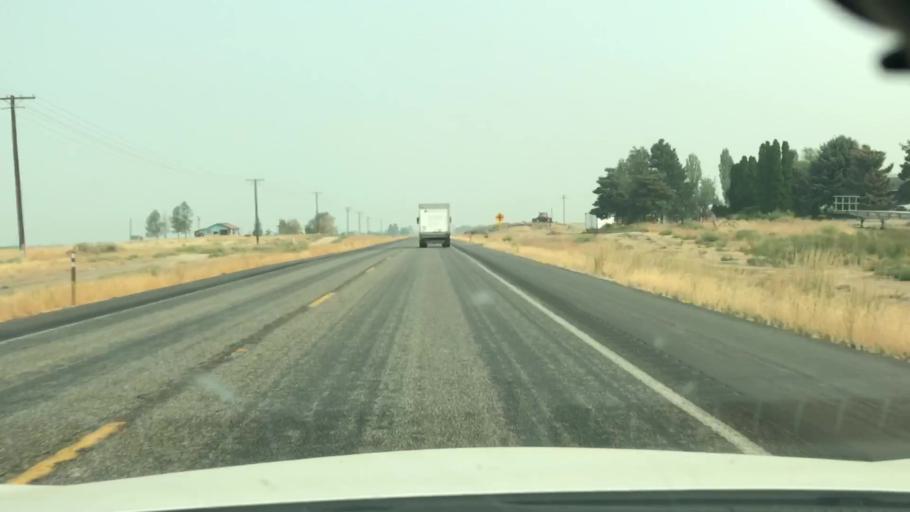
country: US
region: Washington
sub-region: Grant County
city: Quincy
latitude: 47.1295
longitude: -119.8535
